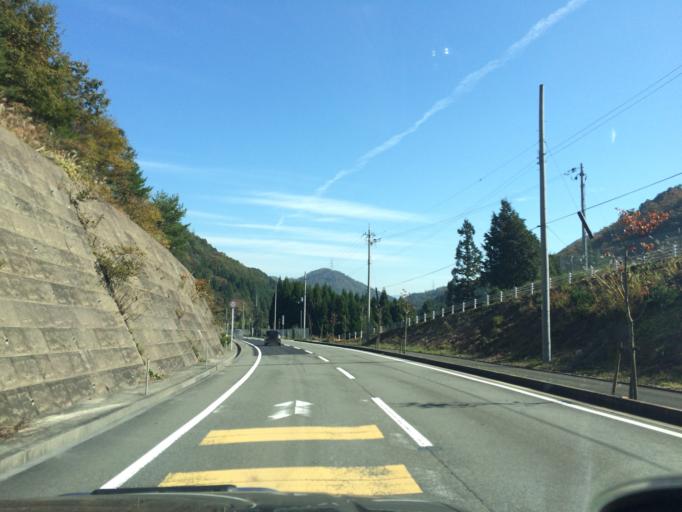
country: JP
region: Hyogo
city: Sasayama
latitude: 35.0676
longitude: 135.3867
